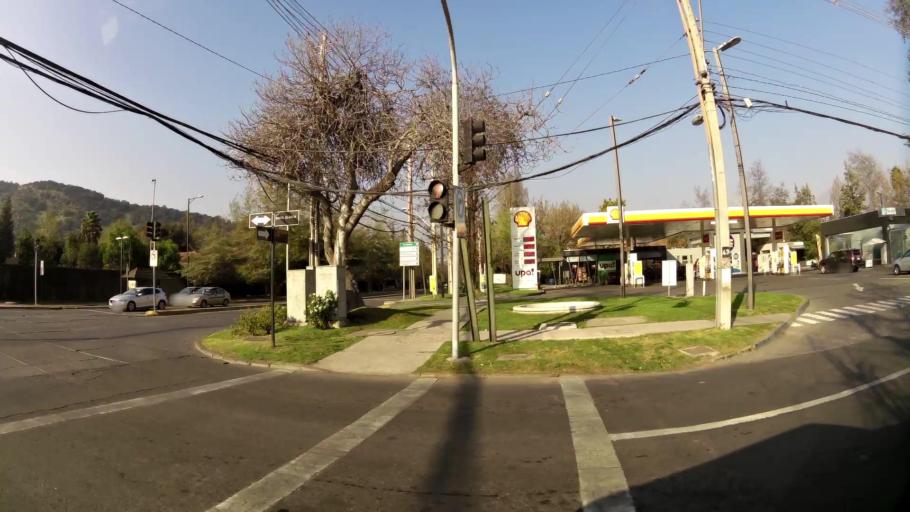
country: CL
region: Santiago Metropolitan
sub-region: Provincia de Santiago
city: Villa Presidente Frei, Nunoa, Santiago, Chile
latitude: -33.3549
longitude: -70.5321
